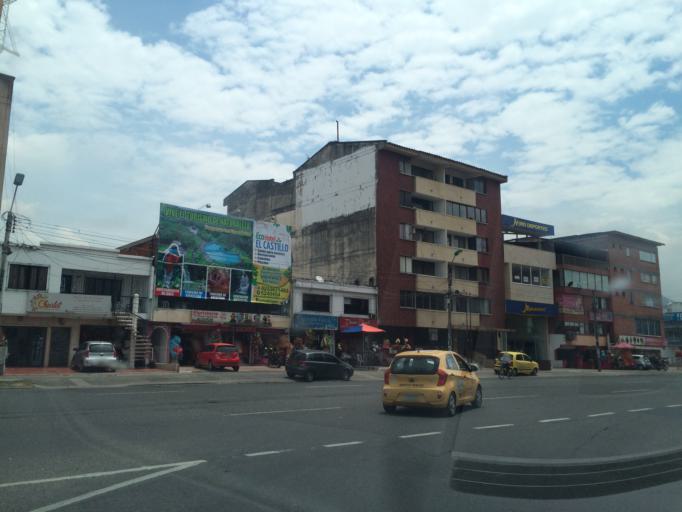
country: CO
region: Valle del Cauca
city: Cali
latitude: 3.4216
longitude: -76.5383
